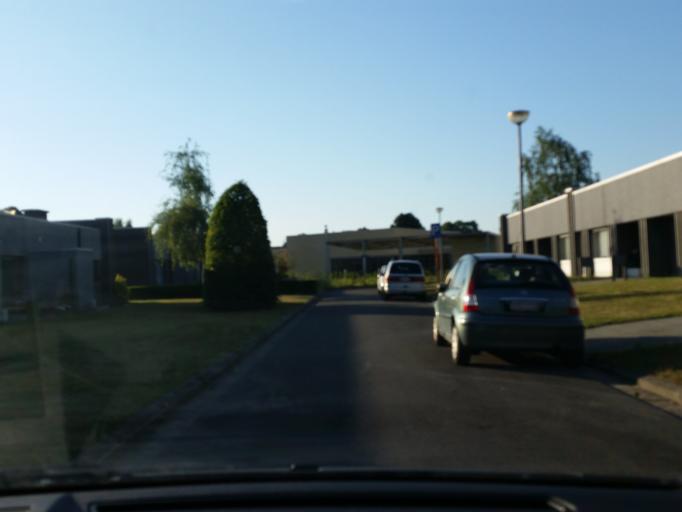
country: BE
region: Flanders
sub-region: Provincie Antwerpen
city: Mechelen
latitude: 51.0000
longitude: 4.4849
